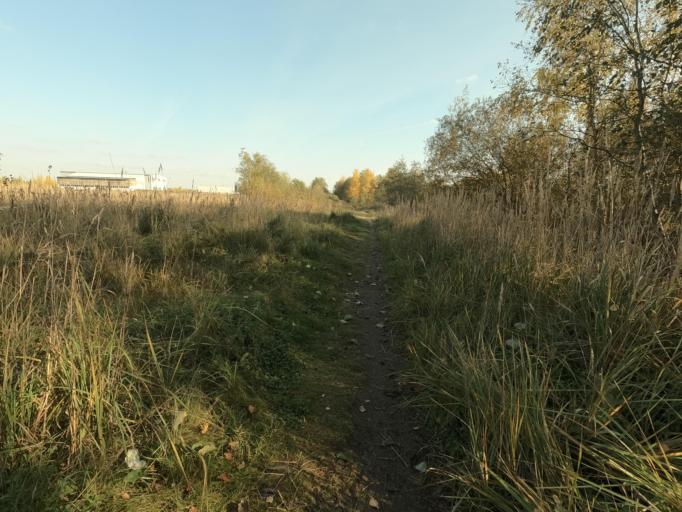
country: RU
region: Leningrad
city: Mga
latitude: 59.7483
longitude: 31.0701
